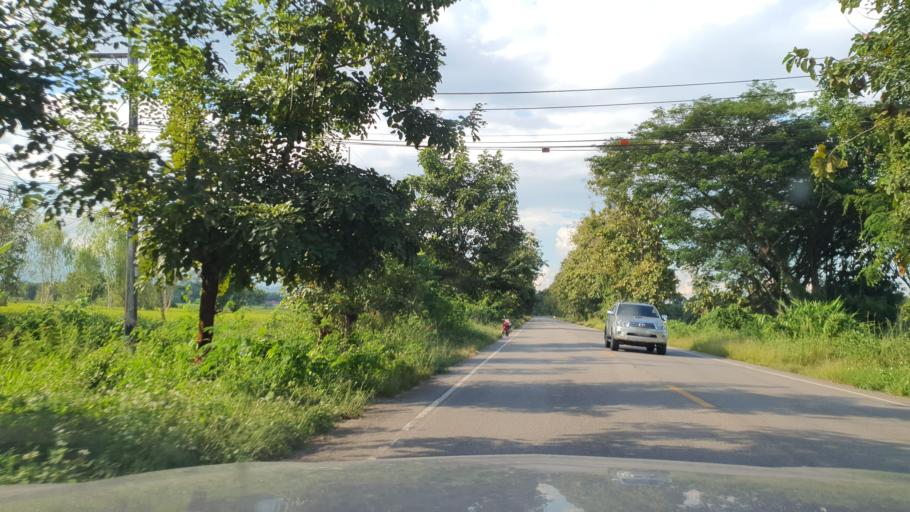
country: TH
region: Phayao
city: Phayao
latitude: 19.1248
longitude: 99.8448
